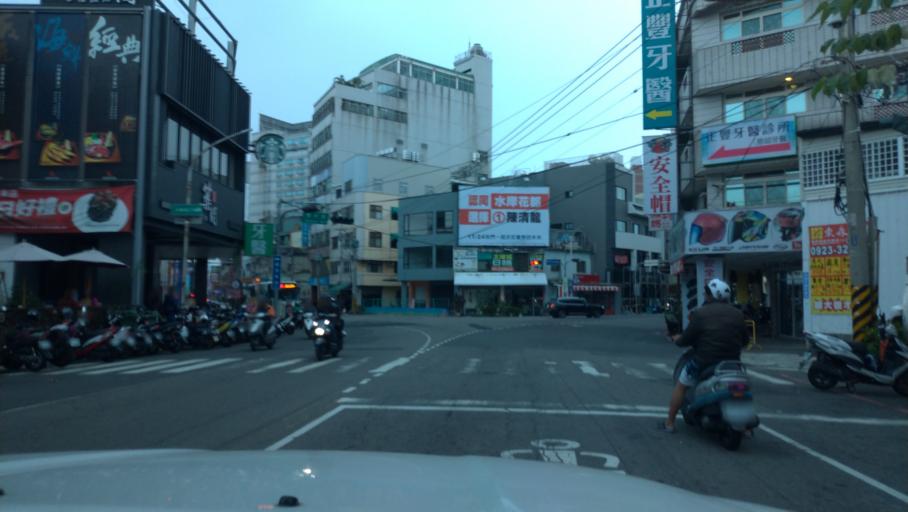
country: TW
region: Taiwan
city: Fengyuan
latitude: 24.2523
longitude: 120.7261
